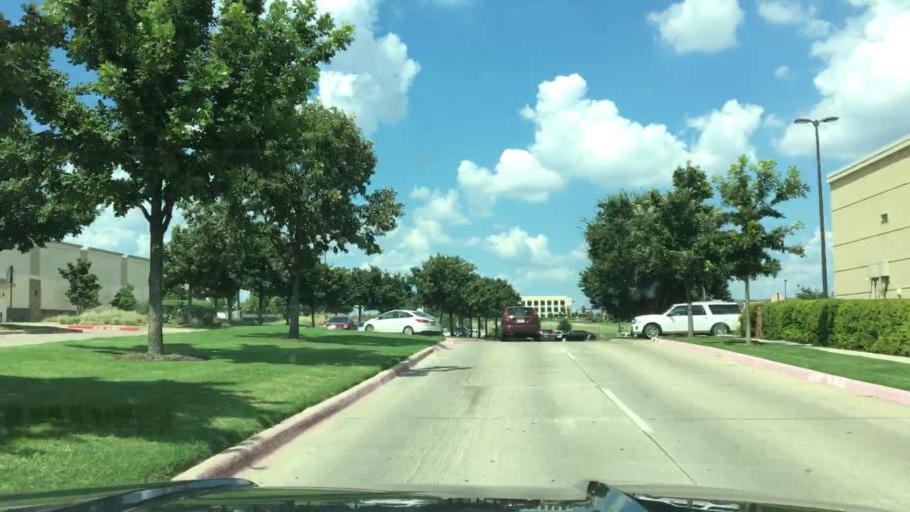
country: US
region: Texas
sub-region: Tarrant County
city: Blue Mound
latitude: 32.9123
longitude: -97.3107
